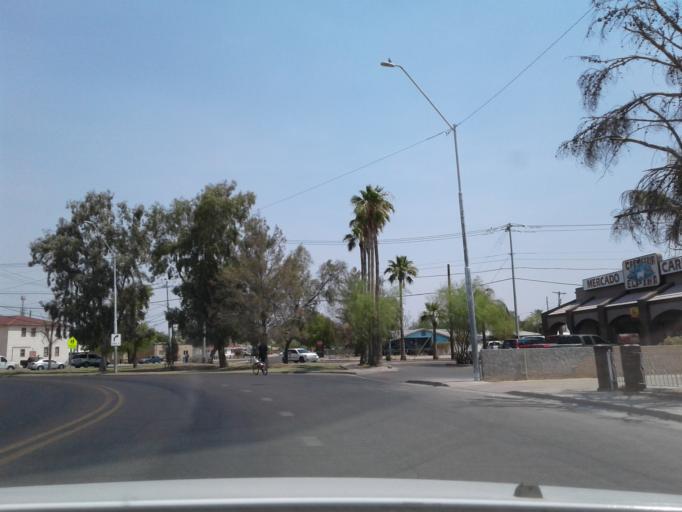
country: US
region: Arizona
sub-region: Pinal County
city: Casa Grande
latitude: 32.8741
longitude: -111.7485
